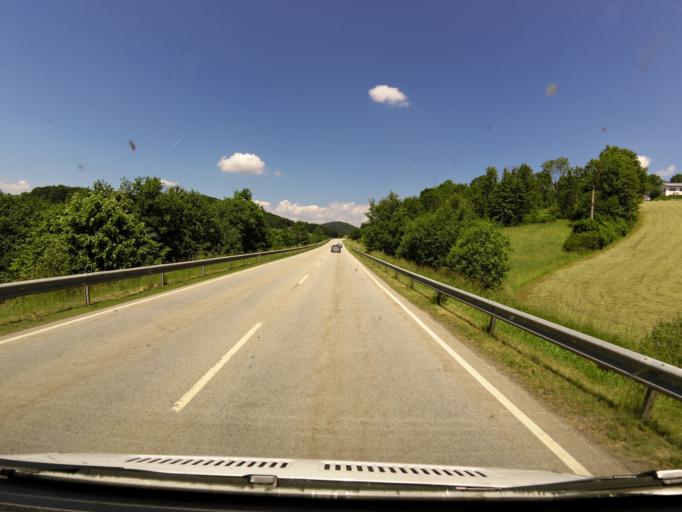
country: DE
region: Bavaria
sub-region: Lower Bavaria
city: Roehrnbach
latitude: 48.7753
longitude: 13.5062
